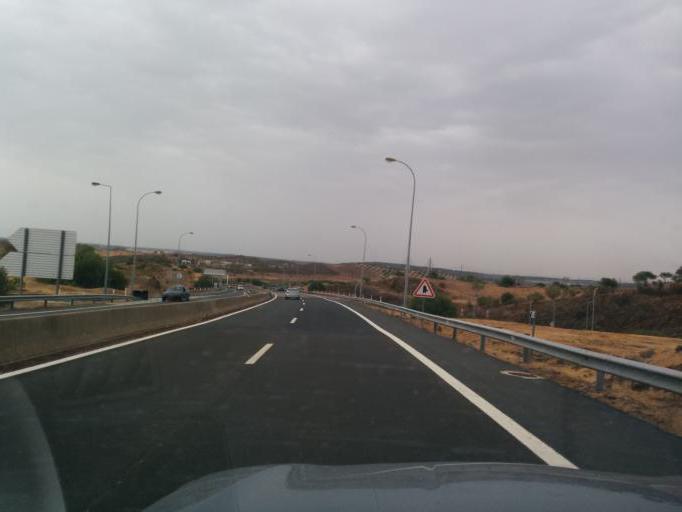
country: PT
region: Faro
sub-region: Castro Marim
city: Castro Marim
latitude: 37.2303
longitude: -7.4496
